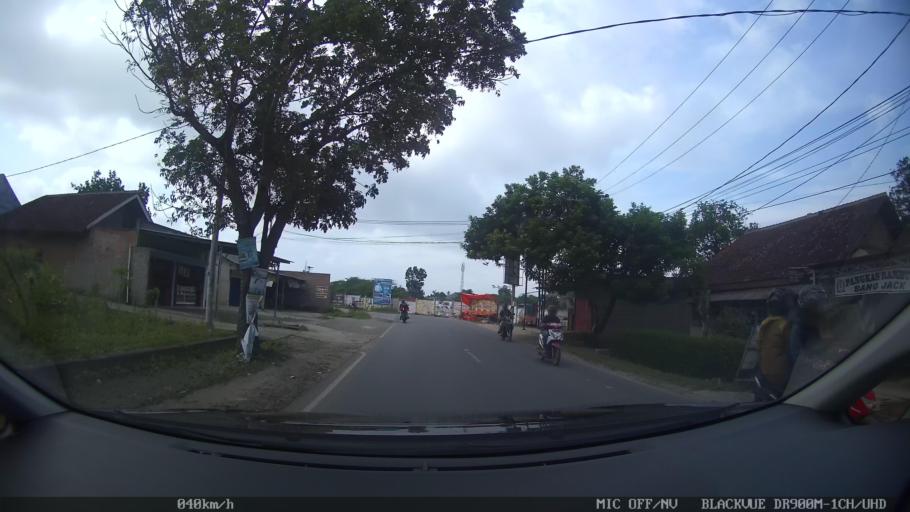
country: ID
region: Lampung
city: Kedaton
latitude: -5.3295
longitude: 105.2903
